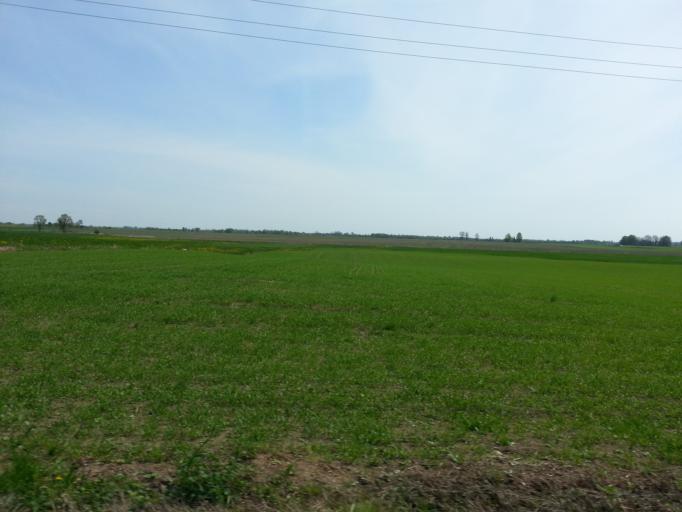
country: LT
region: Panevezys
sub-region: Panevezys City
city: Panevezys
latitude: 55.9101
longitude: 24.2374
